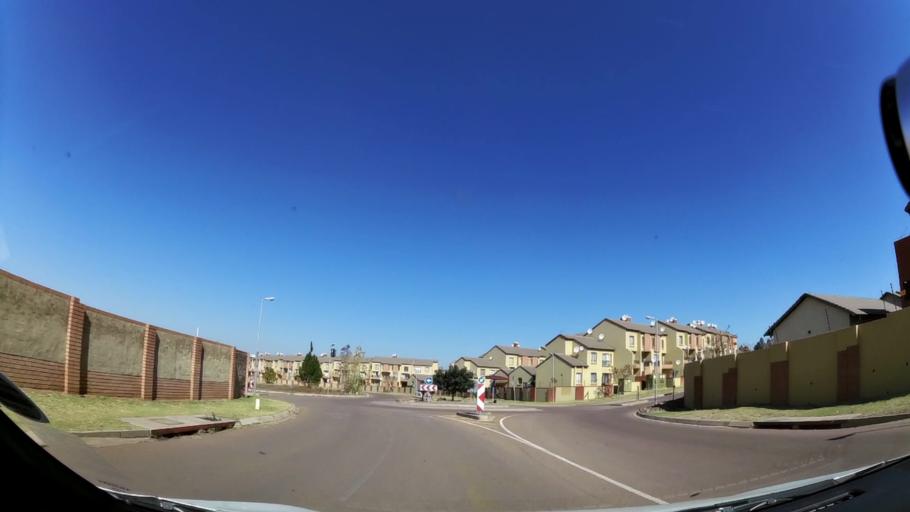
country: ZA
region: Gauteng
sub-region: City of Johannesburg Metropolitan Municipality
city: Midrand
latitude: -25.9502
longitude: 28.1022
